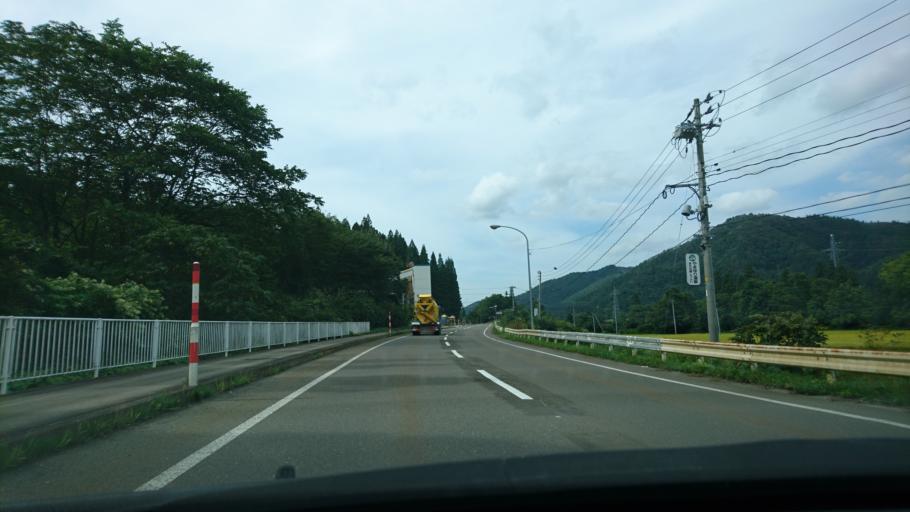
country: JP
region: Akita
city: Yuzawa
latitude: 39.1776
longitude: 140.6594
